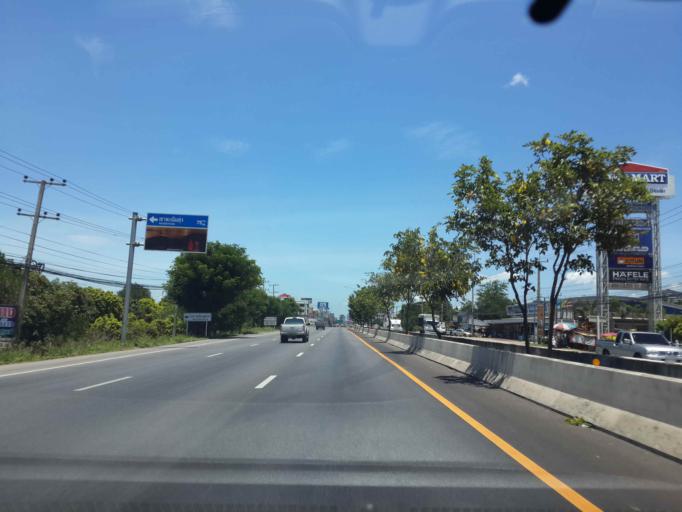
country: TH
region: Phetchaburi
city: Tha Yang
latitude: 12.9612
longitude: 99.9006
